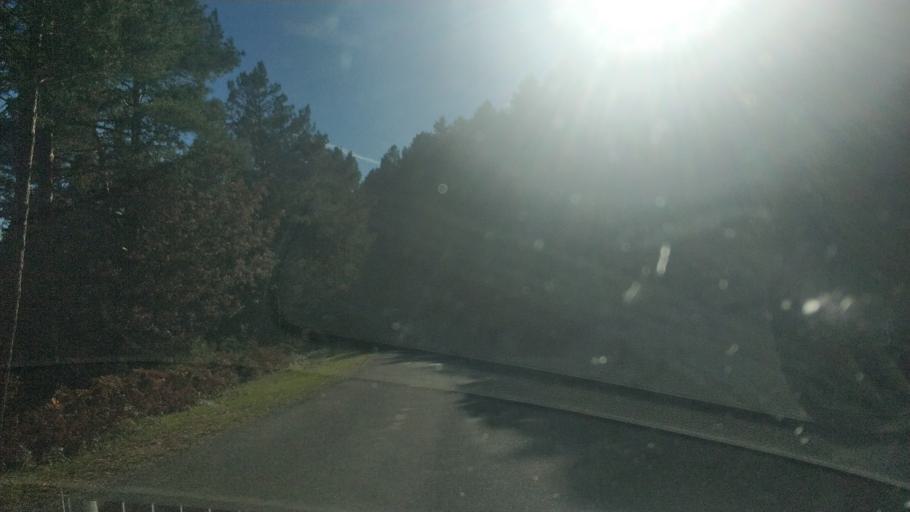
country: ES
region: Castille and Leon
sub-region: Provincia de Soria
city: Vinuesa
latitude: 41.9756
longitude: -2.7947
